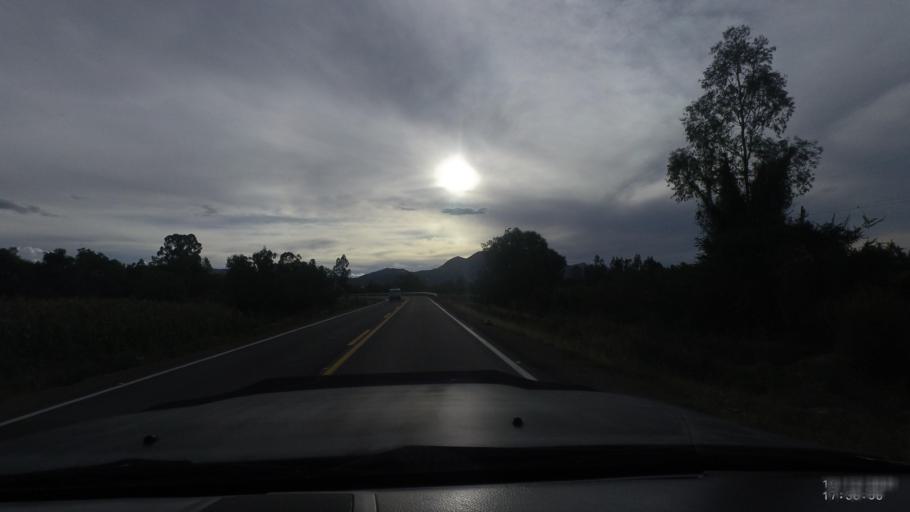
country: BO
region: Cochabamba
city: Tarata
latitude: -17.5750
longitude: -66.0115
